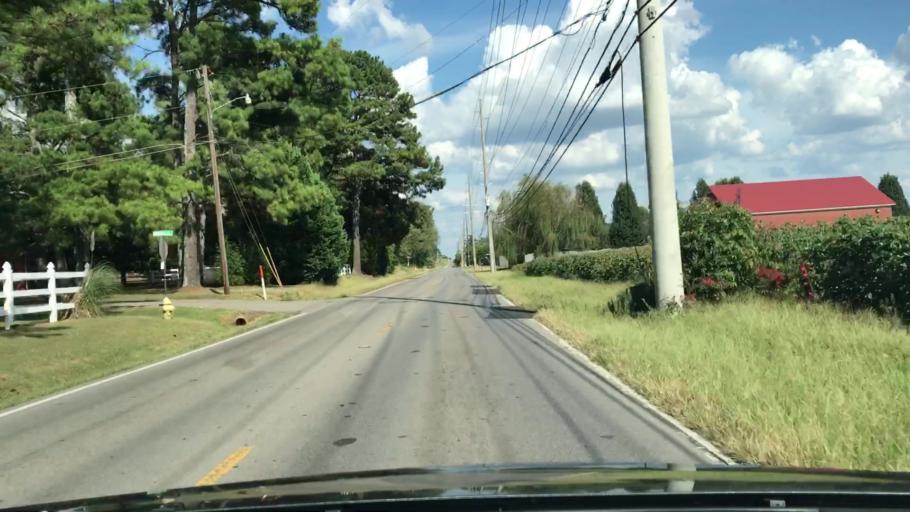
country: US
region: Alabama
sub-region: Madison County
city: Harvest
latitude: 34.8084
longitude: -86.7456
